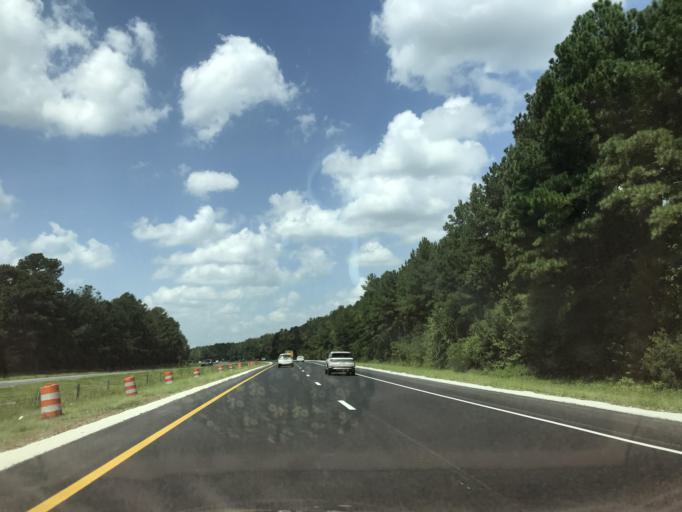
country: US
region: North Carolina
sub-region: Duplin County
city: Warsaw
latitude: 34.9606
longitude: -78.1044
